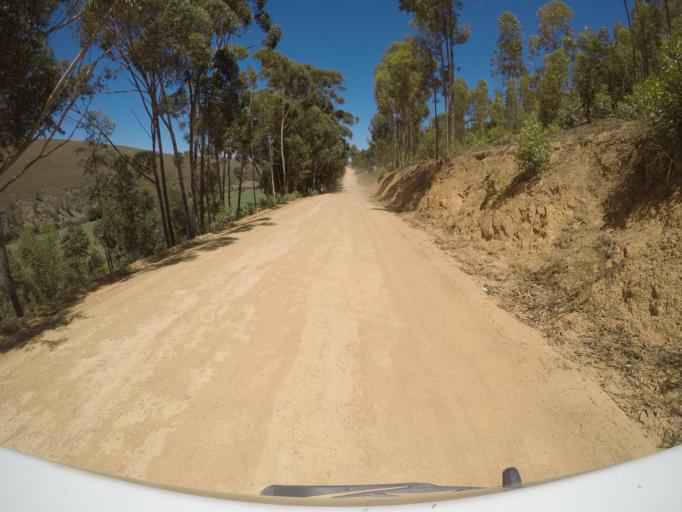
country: ZA
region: Western Cape
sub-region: Overberg District Municipality
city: Grabouw
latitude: -34.2098
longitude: 19.2130
